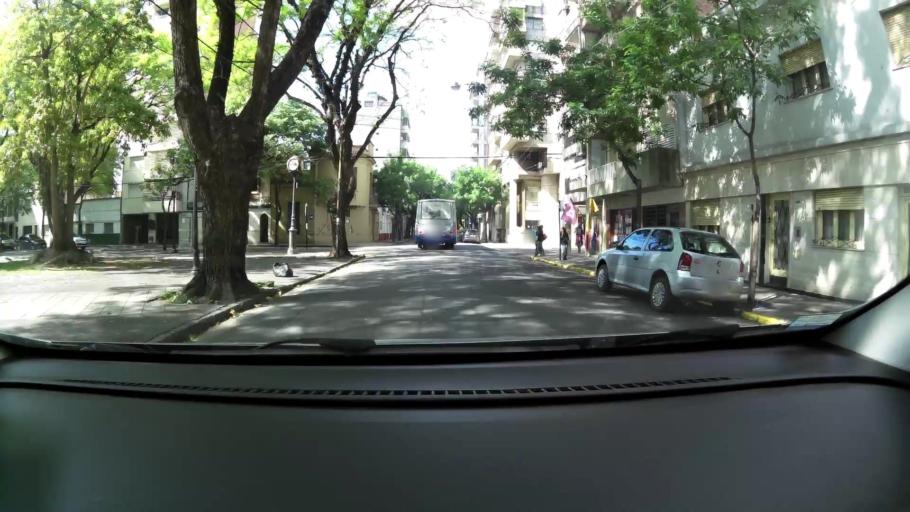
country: AR
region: Santa Fe
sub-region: Departamento de Rosario
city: Rosario
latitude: -32.9570
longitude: -60.6274
